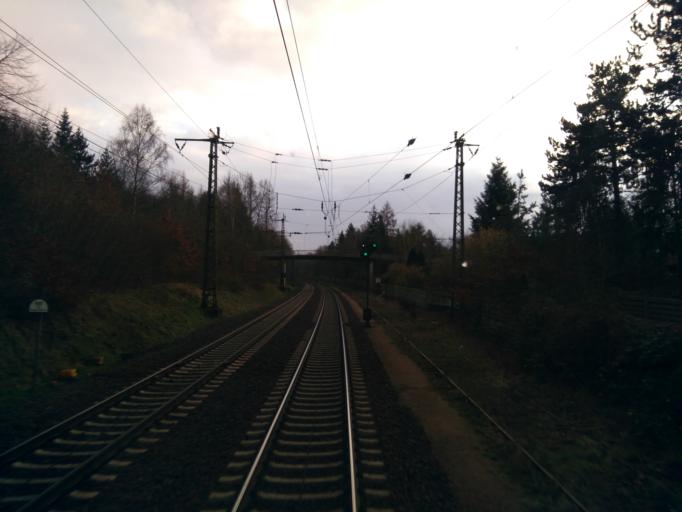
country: DE
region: Lower Saxony
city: Lueneburg
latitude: 53.2313
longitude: 10.4232
